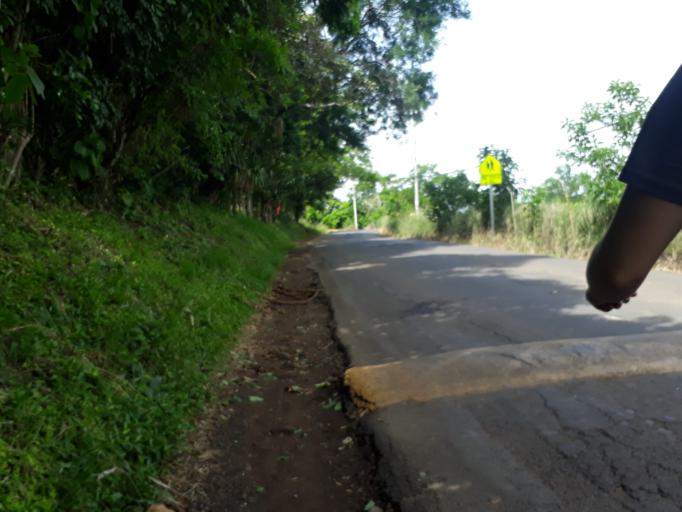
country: CR
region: Alajuela
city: Atenas
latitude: 10.0215
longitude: -84.3407
